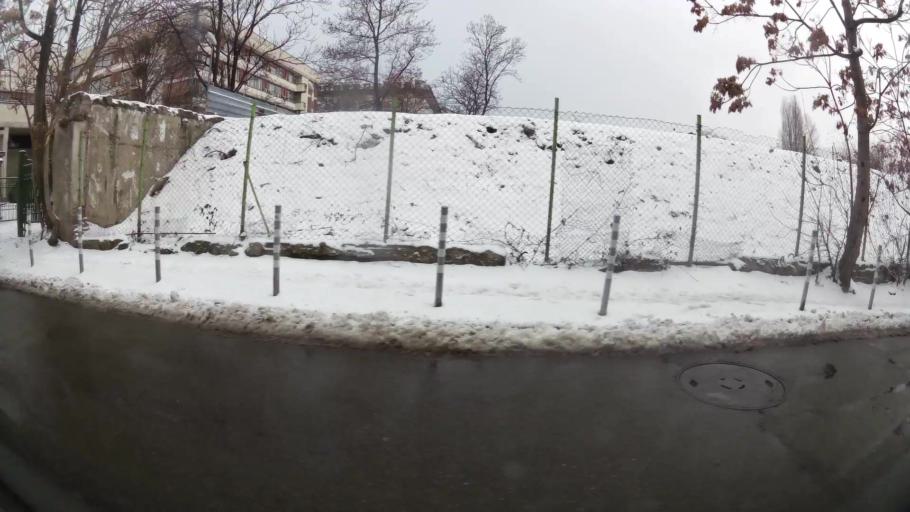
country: BG
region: Sofia-Capital
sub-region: Stolichna Obshtina
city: Sofia
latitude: 42.6919
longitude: 23.3061
